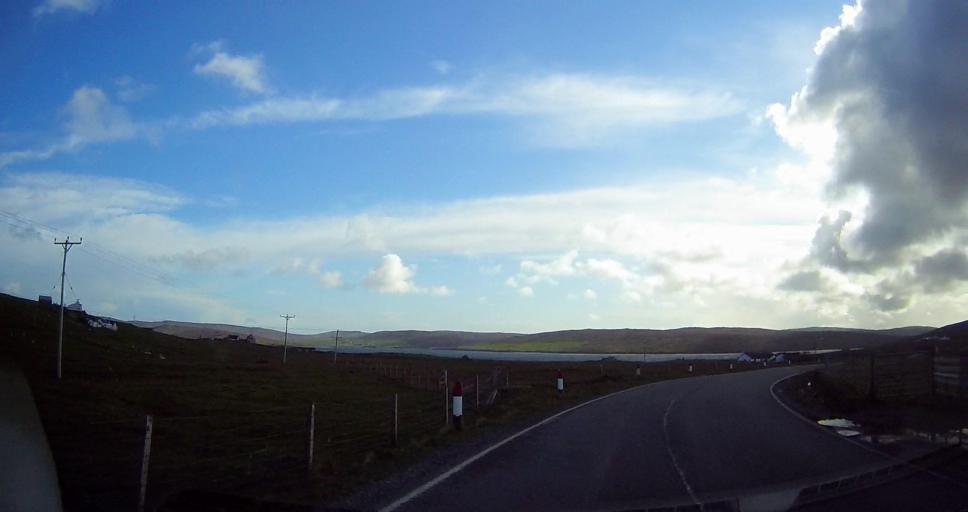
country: GB
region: Scotland
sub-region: Shetland Islands
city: Shetland
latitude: 60.3570
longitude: -1.1462
